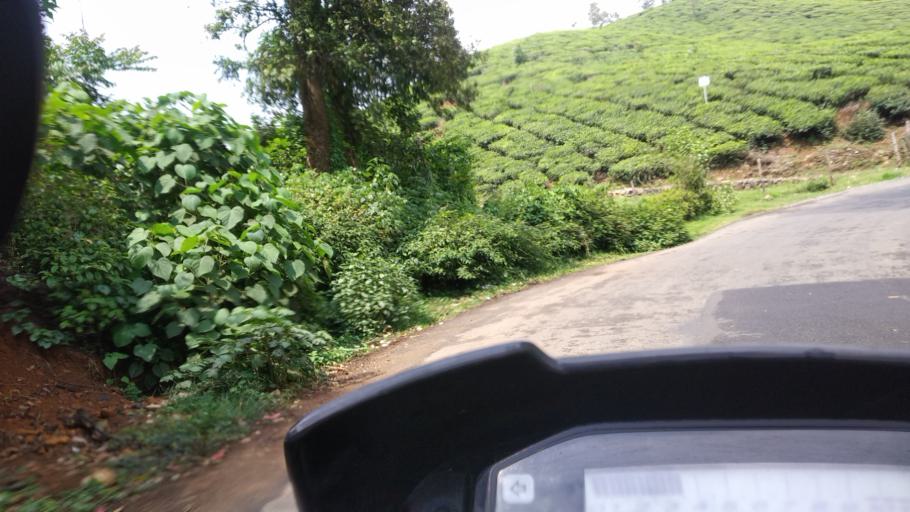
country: IN
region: Kerala
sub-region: Kottayam
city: Erattupetta
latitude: 9.6286
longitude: 76.9659
